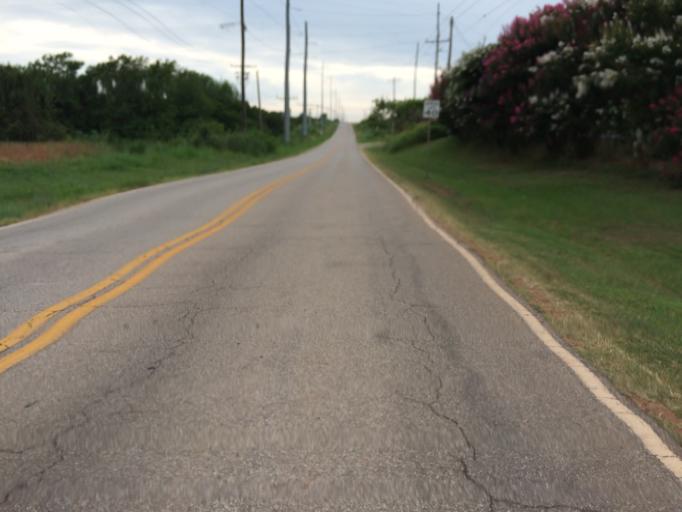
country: US
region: Oklahoma
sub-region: Cleveland County
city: Hall Park
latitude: 35.2474
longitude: -97.4140
